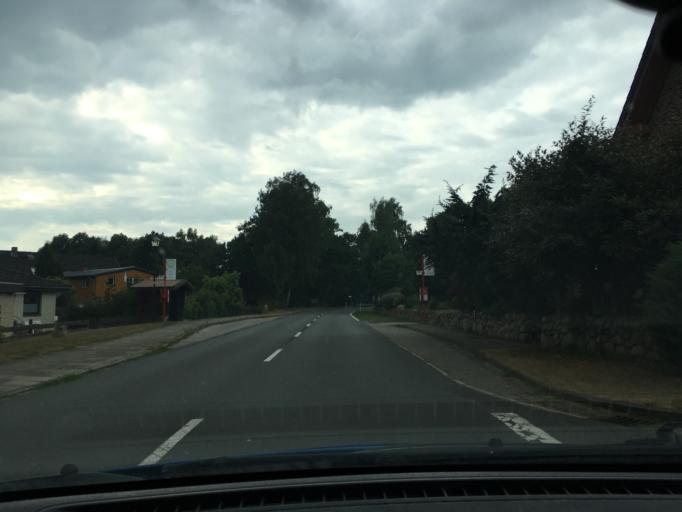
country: DE
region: Lower Saxony
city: Drestedt
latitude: 53.3349
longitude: 9.7577
